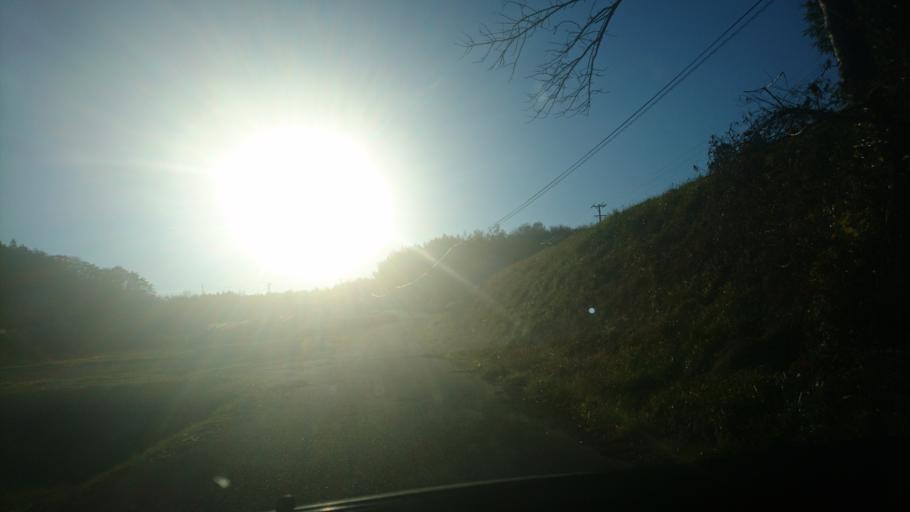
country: JP
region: Iwate
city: Ichinoseki
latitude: 38.9061
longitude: 141.1665
